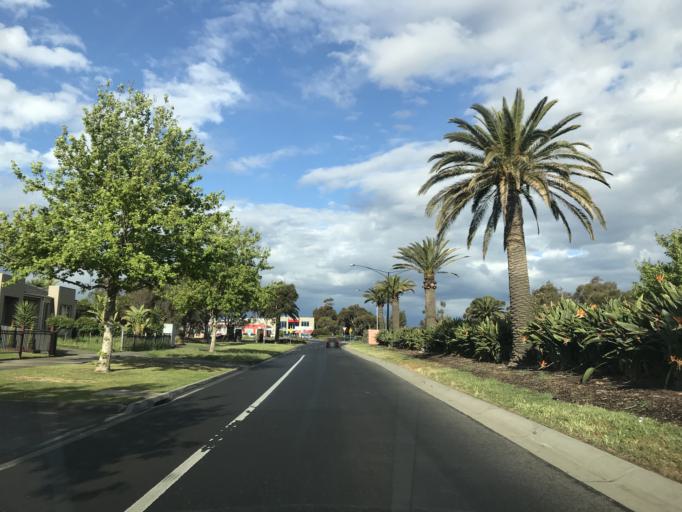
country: AU
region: Victoria
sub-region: Brimbank
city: Derrimut
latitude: -37.7925
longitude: 144.7699
